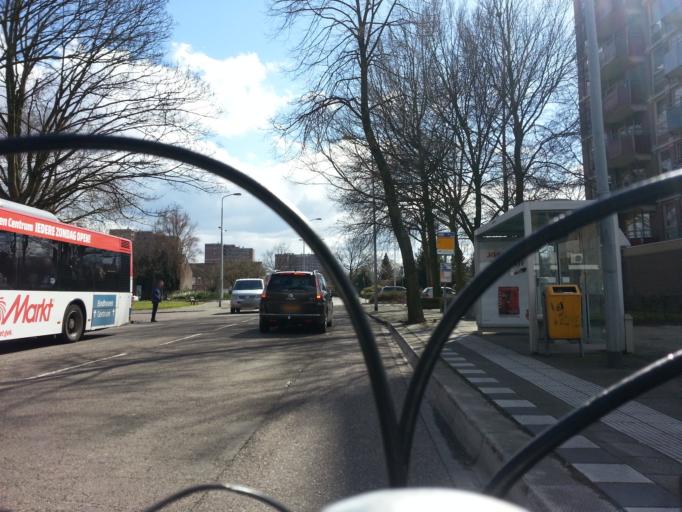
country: NL
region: North Brabant
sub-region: Gemeente Eindhoven
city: Eindhoven
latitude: 51.4581
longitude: 5.4827
